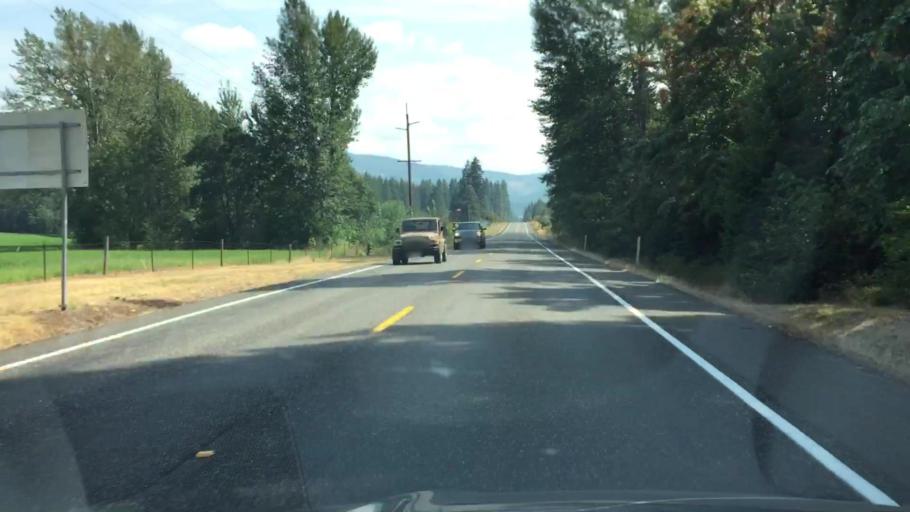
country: US
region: Washington
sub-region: Klickitat County
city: White Salmon
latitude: 45.8457
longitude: -121.5062
